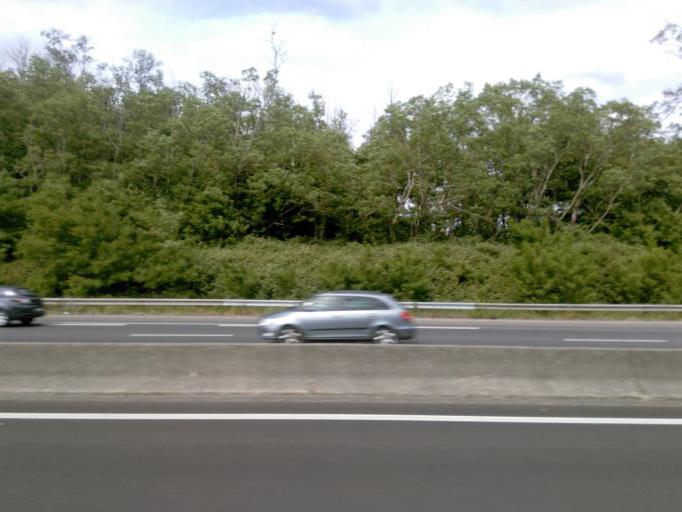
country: FR
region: Ile-de-France
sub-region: Departement du Val-d'Oise
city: Pierrelaye
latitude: 49.0065
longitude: 2.1634
